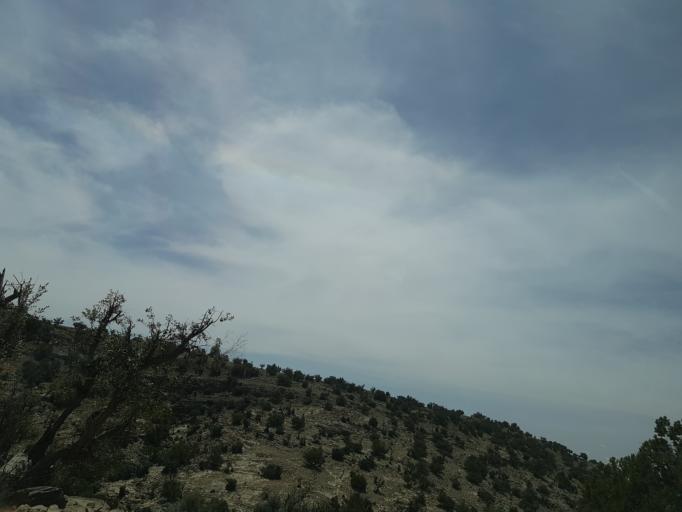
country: OM
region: Al Batinah
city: Bayt al `Awabi
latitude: 23.1366
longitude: 57.5957
